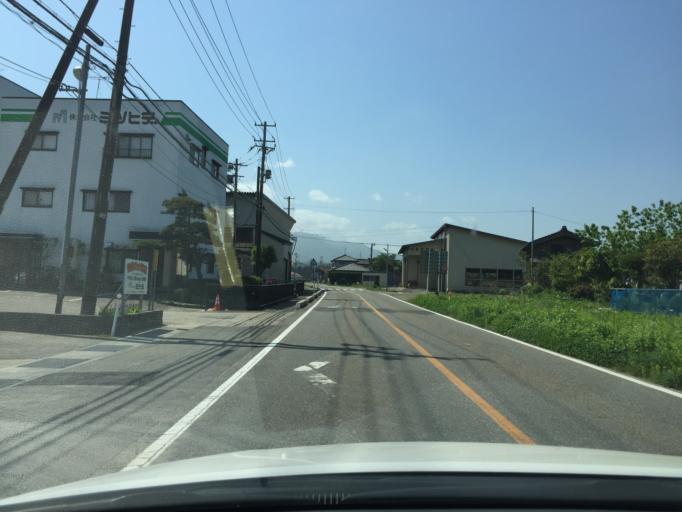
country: JP
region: Niigata
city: Muramatsu
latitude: 37.6863
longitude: 139.1515
